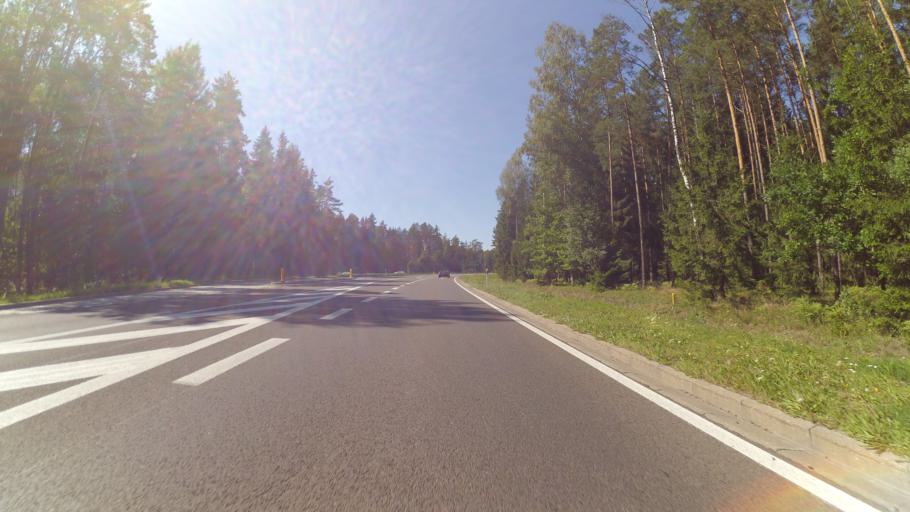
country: PL
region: Podlasie
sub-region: Powiat bialostocki
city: Suprasl
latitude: 53.1267
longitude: 23.4206
